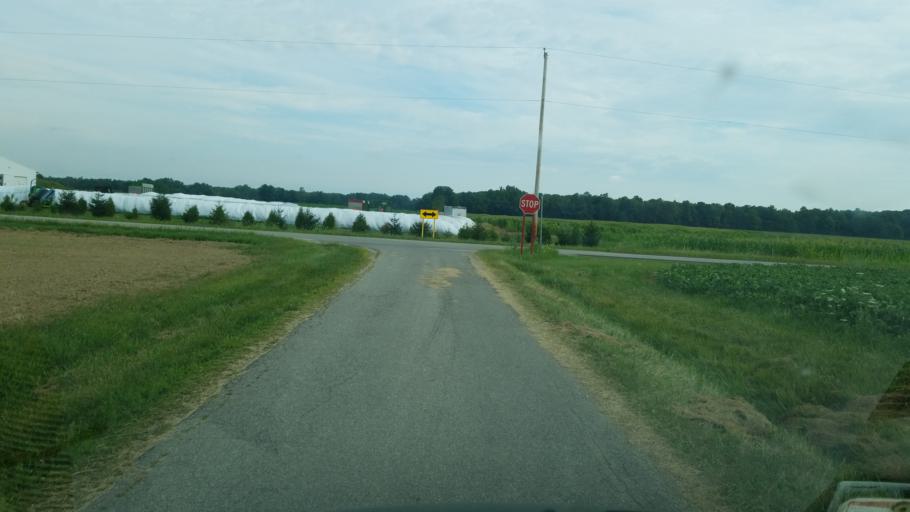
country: US
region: Ohio
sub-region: Crawford County
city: Bucyrus
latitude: 40.9500
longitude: -83.0356
